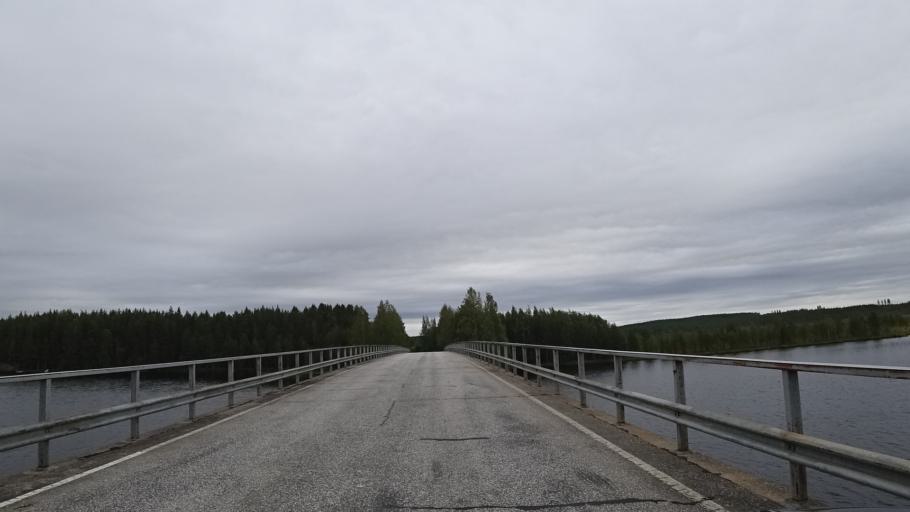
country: FI
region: North Karelia
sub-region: Pielisen Karjala
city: Lieksa
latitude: 63.3465
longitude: 30.2637
